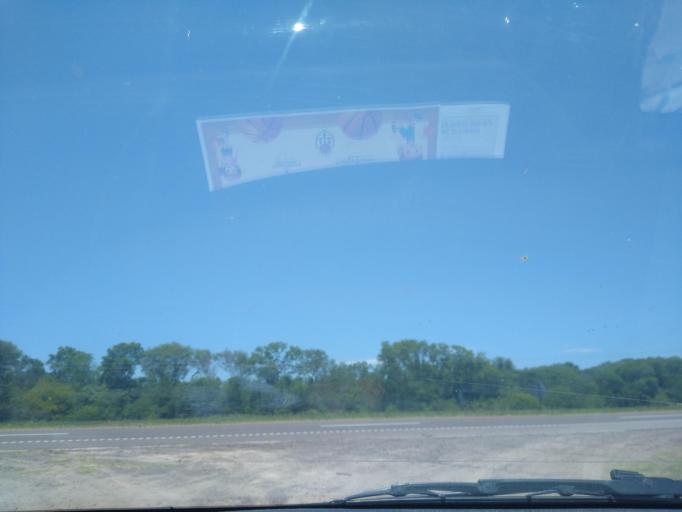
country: AR
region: Chaco
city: Makalle
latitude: -27.2528
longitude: -59.1649
